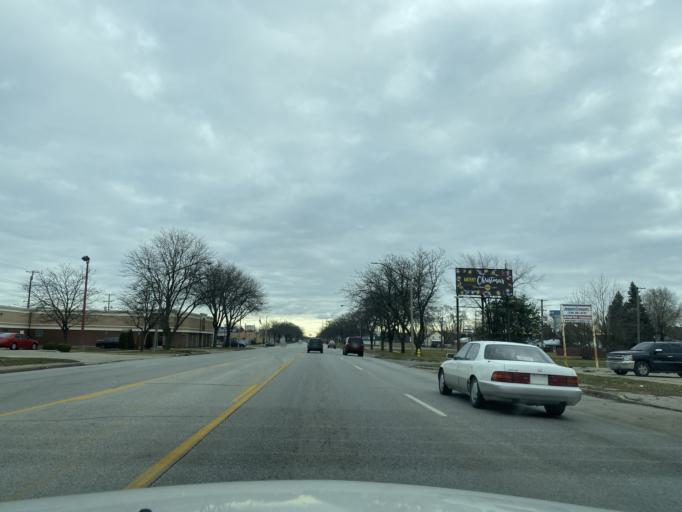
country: US
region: Michigan
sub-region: Wayne County
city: Southgate
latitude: 42.1996
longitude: -83.1721
